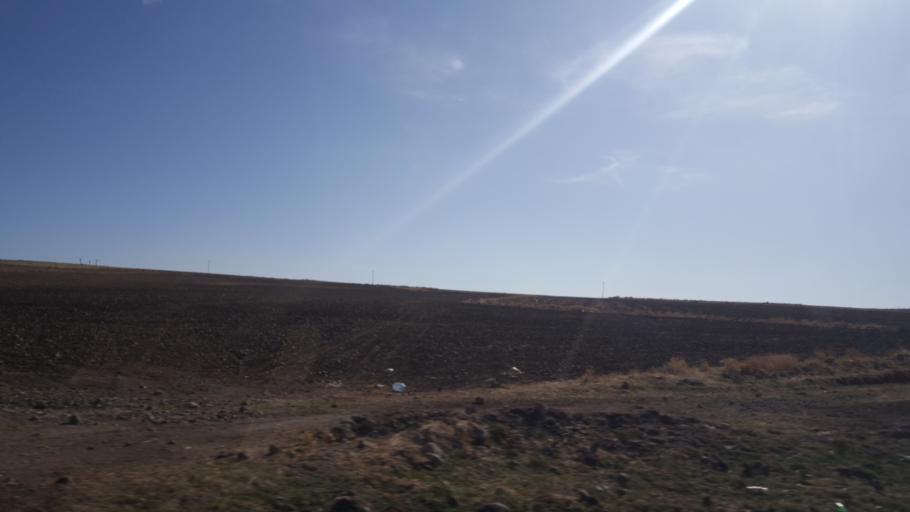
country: TR
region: Ankara
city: Altpinar
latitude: 39.2415
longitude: 32.7258
